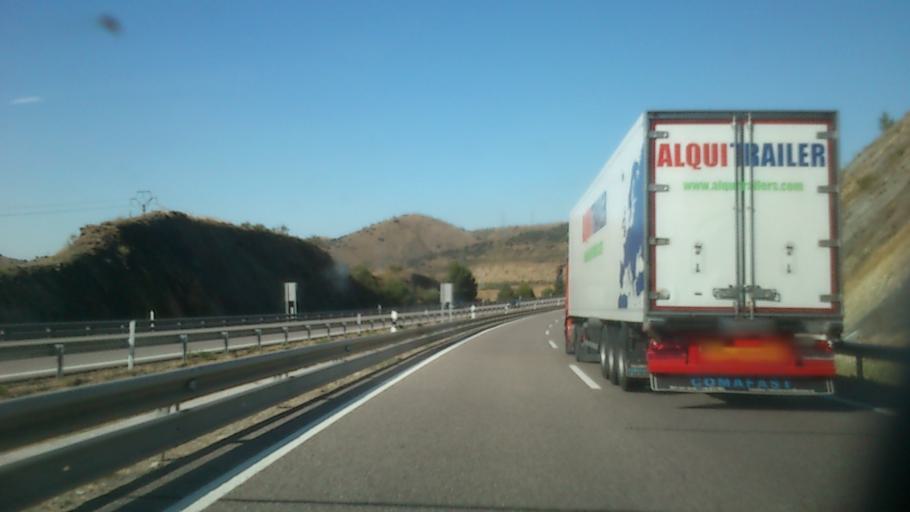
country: ES
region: Aragon
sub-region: Provincia de Zaragoza
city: Paracuellos de la Ribera
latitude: 41.3994
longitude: -1.5451
